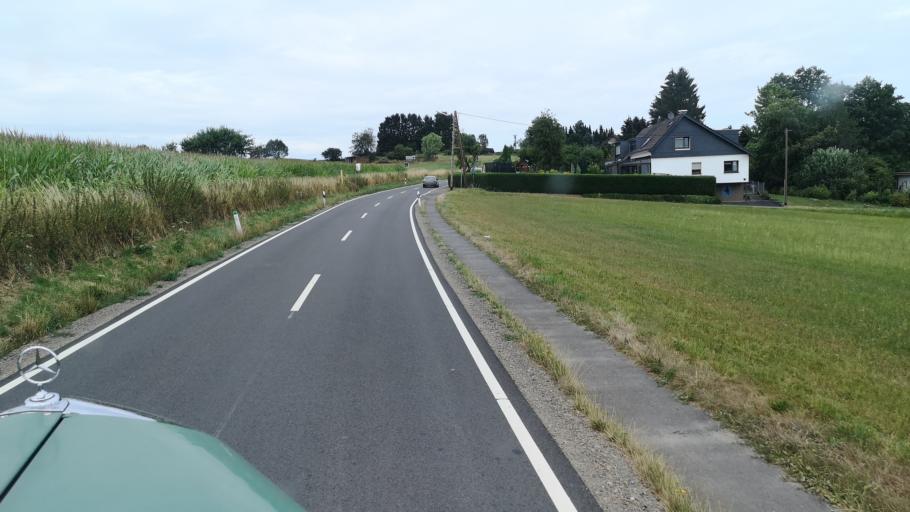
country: DE
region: North Rhine-Westphalia
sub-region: Regierungsbezirk Koln
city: Odenthal
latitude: 51.0556
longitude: 7.1694
